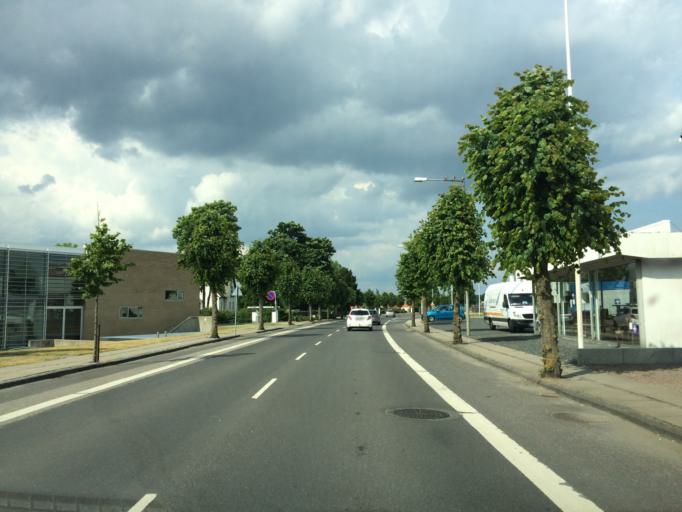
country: DK
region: South Denmark
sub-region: Middelfart Kommune
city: Middelfart
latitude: 55.5068
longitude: 9.7515
